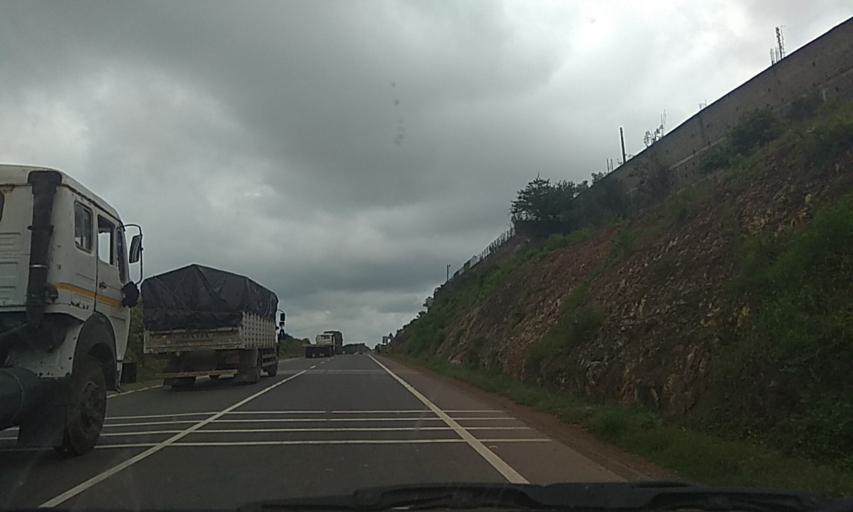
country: IN
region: Karnataka
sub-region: Dharwad
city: Hubli
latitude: 15.3605
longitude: 75.0503
